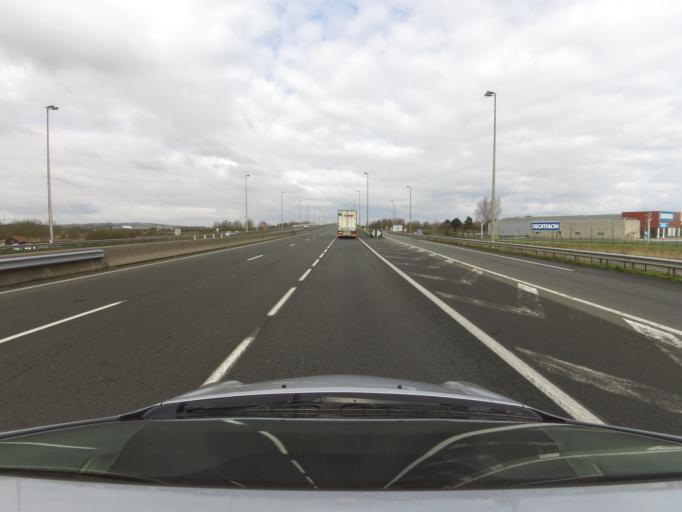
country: FR
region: Nord-Pas-de-Calais
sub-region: Departement du Pas-de-Calais
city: Calais
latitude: 50.9380
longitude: 1.8415
